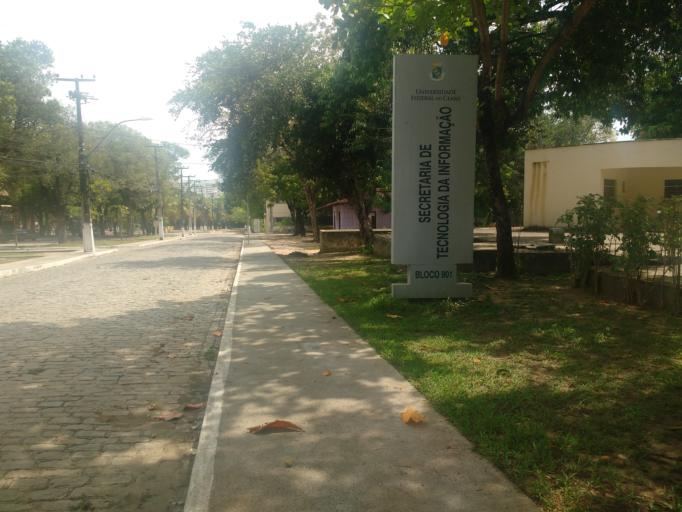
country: BR
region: Ceara
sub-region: Fortaleza
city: Fortaleza
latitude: -3.7450
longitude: -38.5760
